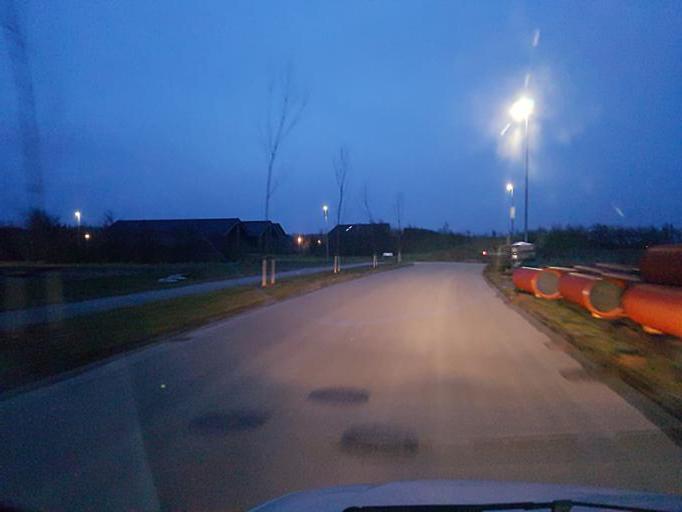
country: DK
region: South Denmark
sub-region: Esbjerg Kommune
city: Bramming
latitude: 55.4764
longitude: 8.6814
